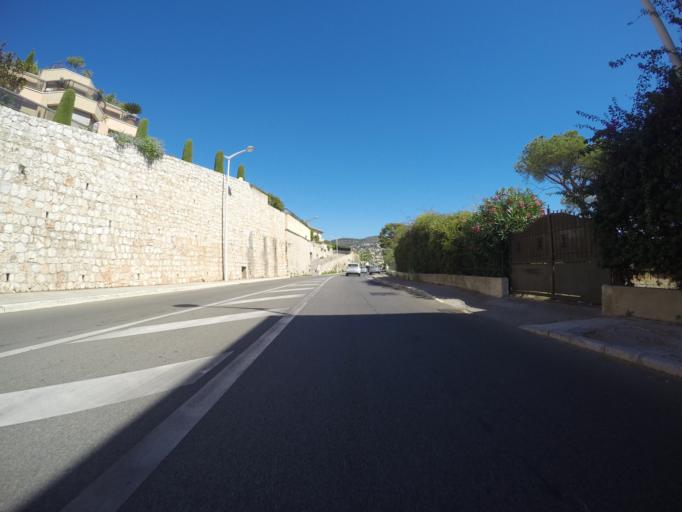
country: FR
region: Provence-Alpes-Cote d'Azur
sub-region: Departement des Alpes-Maritimes
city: Villefranche-sur-Mer
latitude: 43.6894
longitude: 7.3071
